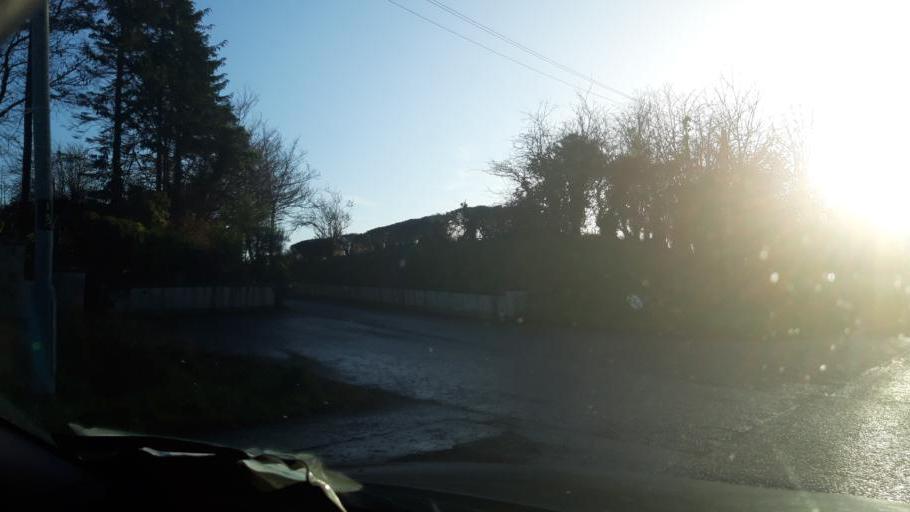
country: GB
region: Northern Ireland
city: Garvagh
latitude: 54.9933
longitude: -6.6821
